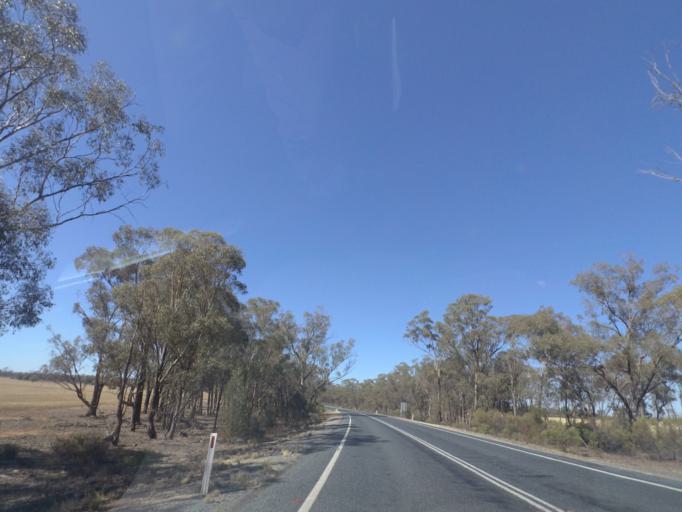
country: AU
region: New South Wales
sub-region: Bland
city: West Wyalong
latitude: -34.1194
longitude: 147.1283
